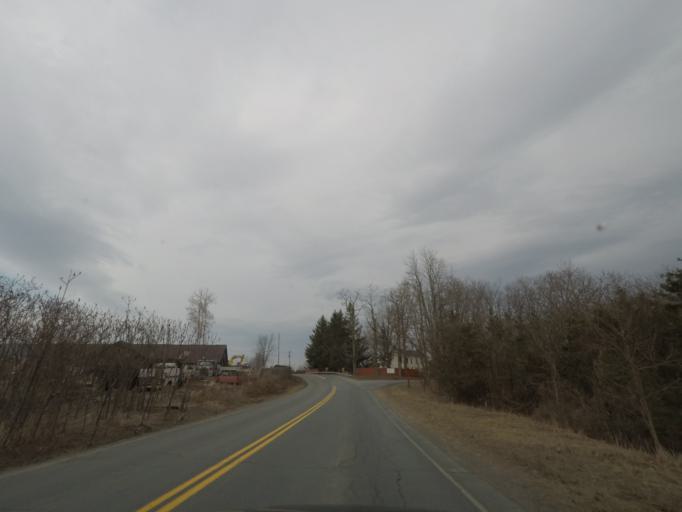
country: US
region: New York
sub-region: Washington County
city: Cambridge
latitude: 42.9373
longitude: -73.4932
